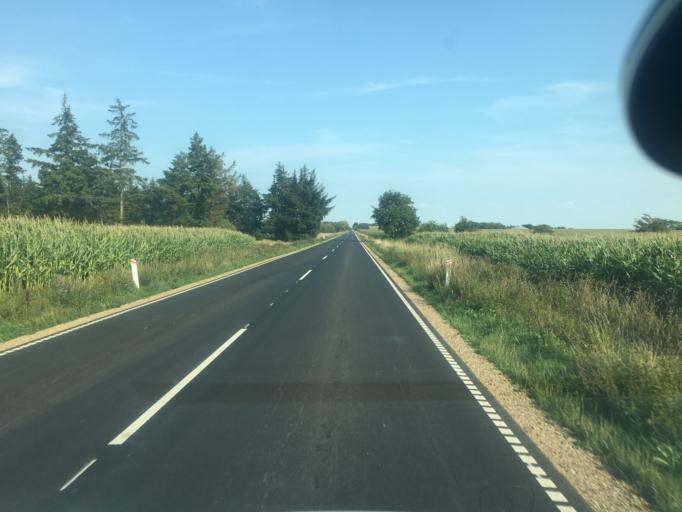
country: DK
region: South Denmark
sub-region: Tonder Kommune
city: Logumkloster
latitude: 55.0022
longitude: 8.9102
